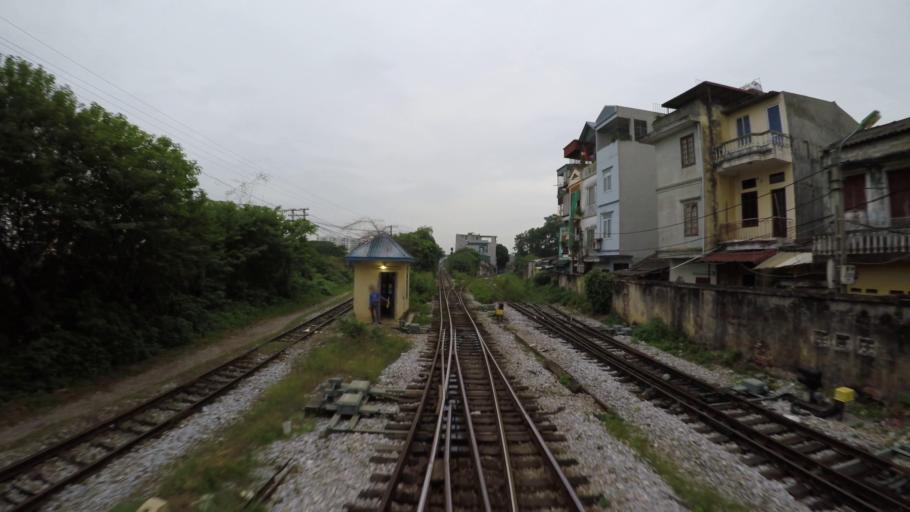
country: VN
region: Ha Noi
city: Trau Quy
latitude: 21.0232
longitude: 105.9316
